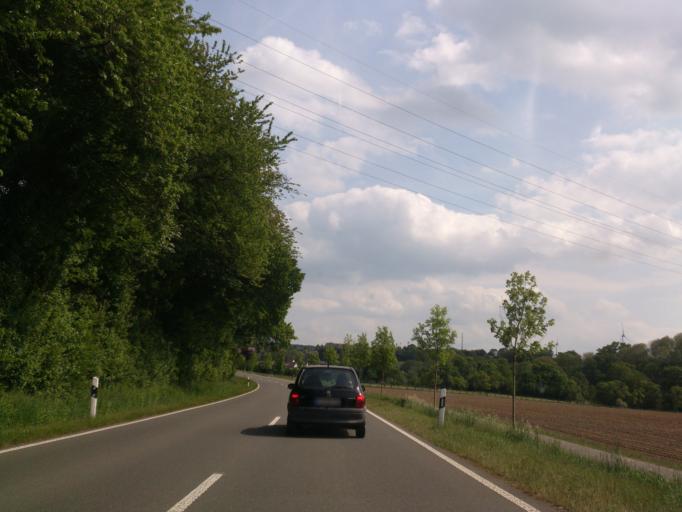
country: DE
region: North Rhine-Westphalia
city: Bad Lippspringe
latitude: 51.7489
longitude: 8.8373
